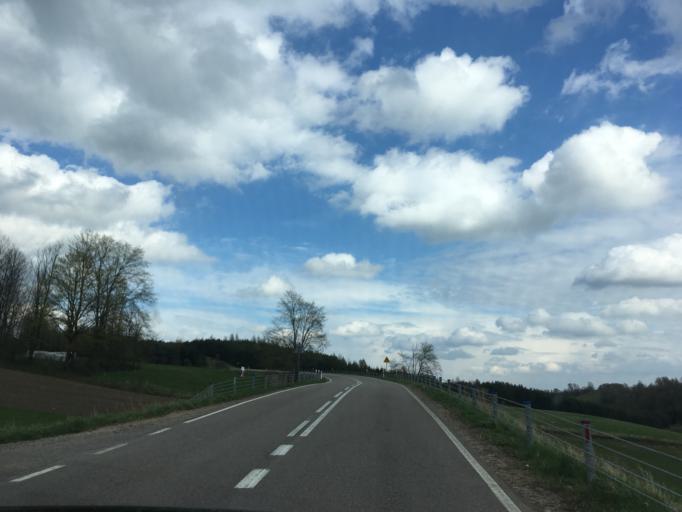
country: PL
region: Podlasie
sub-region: Powiat suwalski
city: Filipow
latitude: 54.3592
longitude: 22.8096
